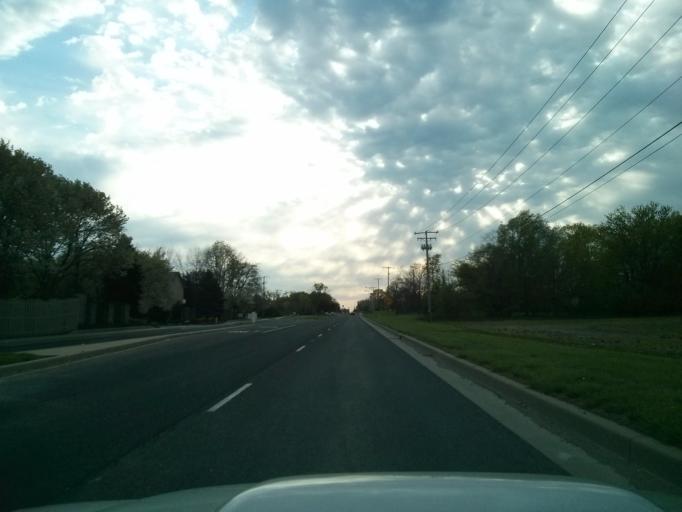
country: US
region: Indiana
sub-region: Hamilton County
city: Carmel
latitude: 40.0003
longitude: -86.0731
